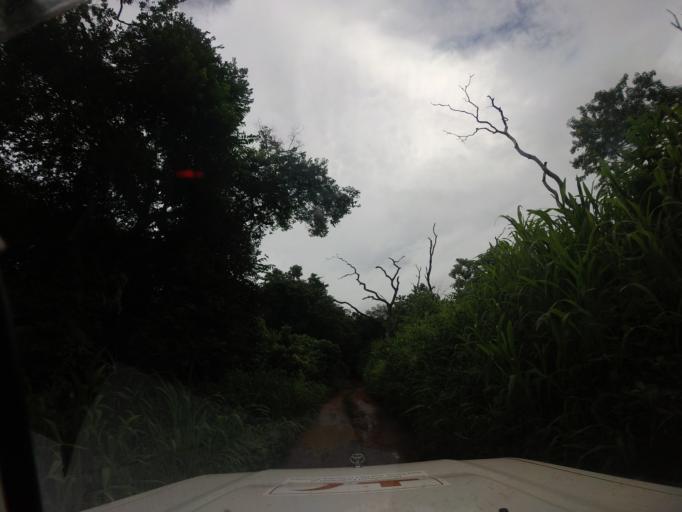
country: SL
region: Northern Province
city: Kamakwie
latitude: 9.6490
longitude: -12.2182
